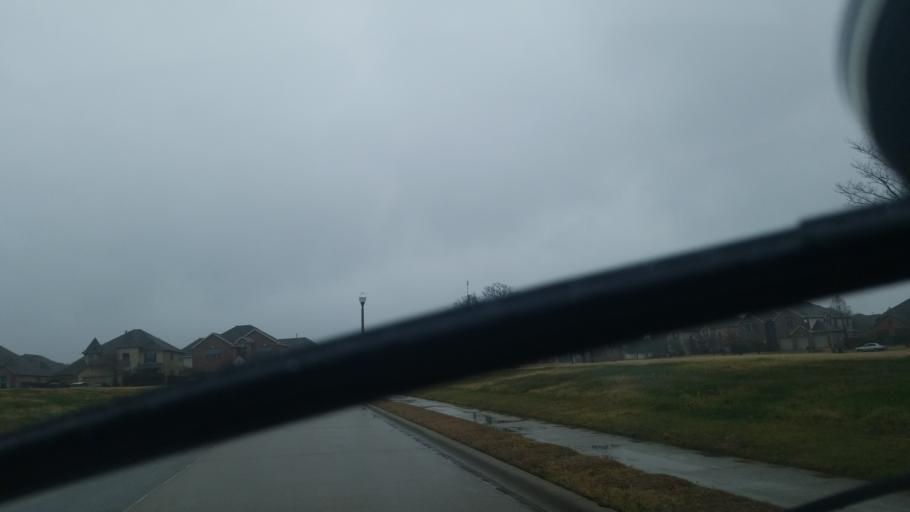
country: US
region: Texas
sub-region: Denton County
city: Corinth
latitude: 33.1770
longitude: -97.0586
